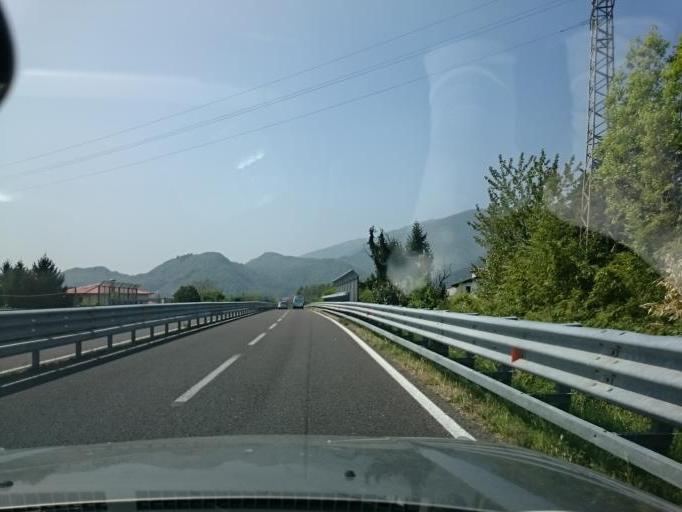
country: IT
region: Veneto
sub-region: Provincia di Vicenza
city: Pove del Grappa
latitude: 45.7890
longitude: 11.7430
